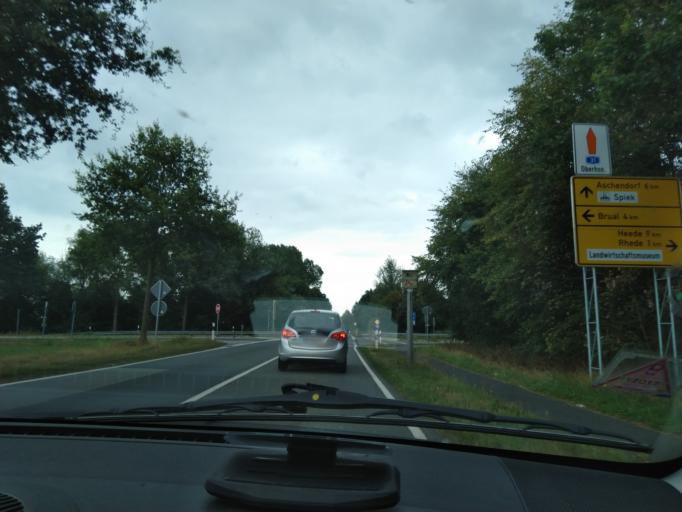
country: DE
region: Lower Saxony
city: Rhede
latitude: 53.0644
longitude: 7.2675
